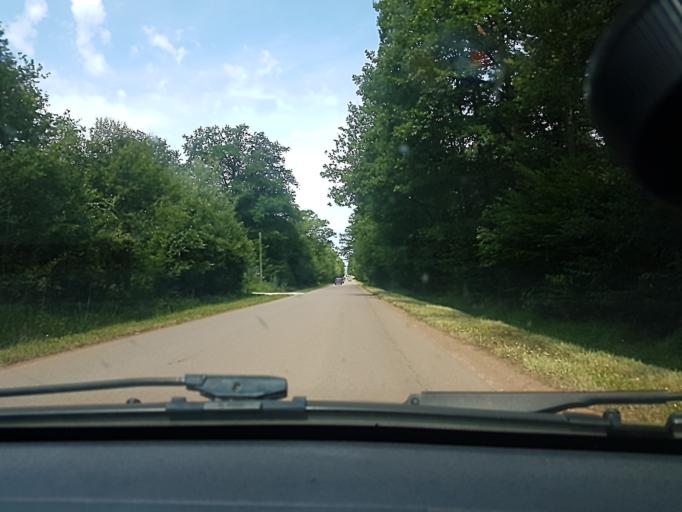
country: FR
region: Bourgogne
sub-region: Departement de Saone-et-Loire
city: Chagny
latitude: 46.8909
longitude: 4.7951
